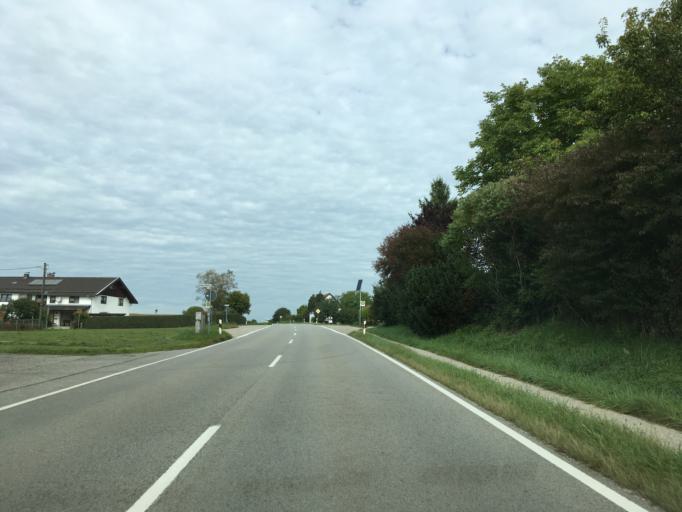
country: DE
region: Bavaria
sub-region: Upper Bavaria
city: Eiselfing
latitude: 48.0160
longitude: 12.2407
